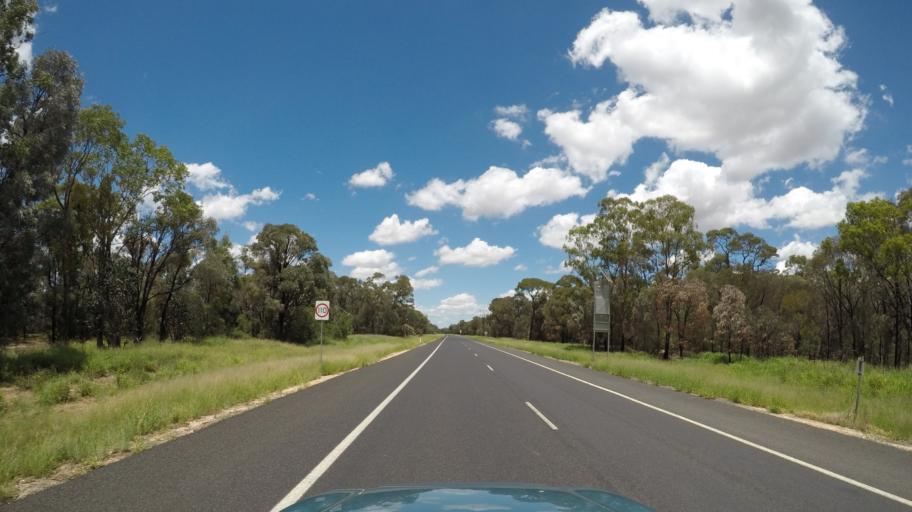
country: AU
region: Queensland
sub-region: Goondiwindi
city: Goondiwindi
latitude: -28.0810
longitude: 150.7392
